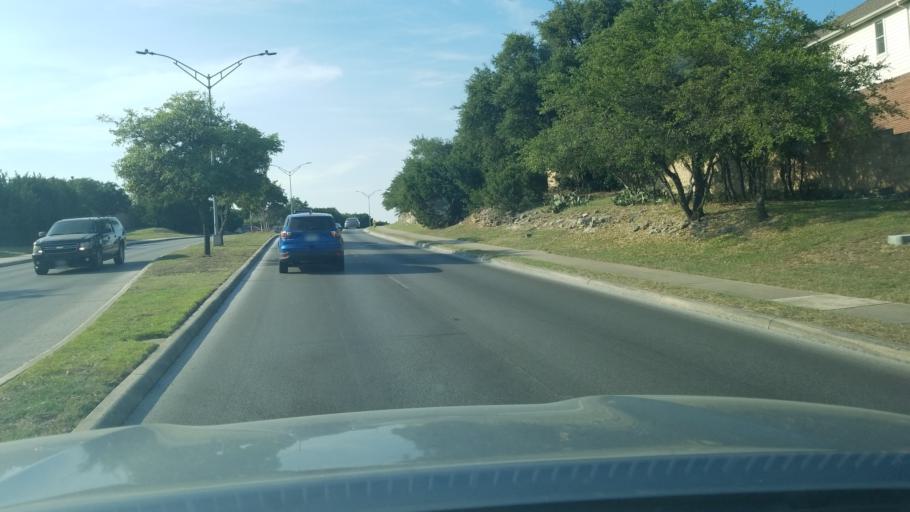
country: US
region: Texas
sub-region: Bexar County
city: Hollywood Park
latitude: 29.6400
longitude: -98.5066
